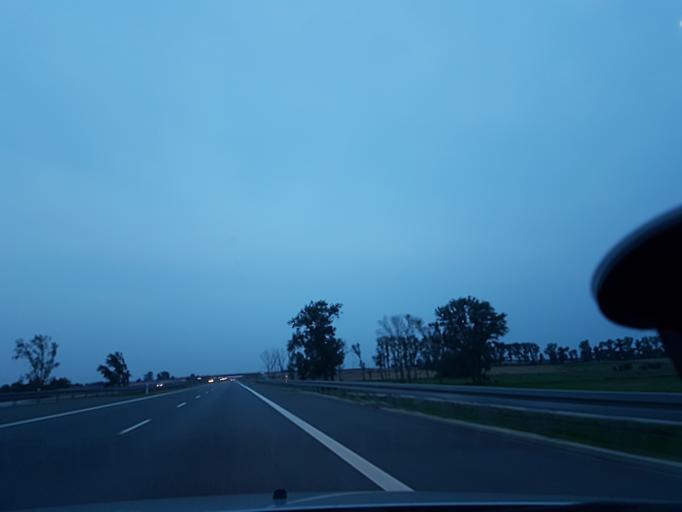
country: PL
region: Lodz Voivodeship
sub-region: Powiat kutnowski
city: Krzyzanow
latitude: 52.1754
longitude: 19.4857
